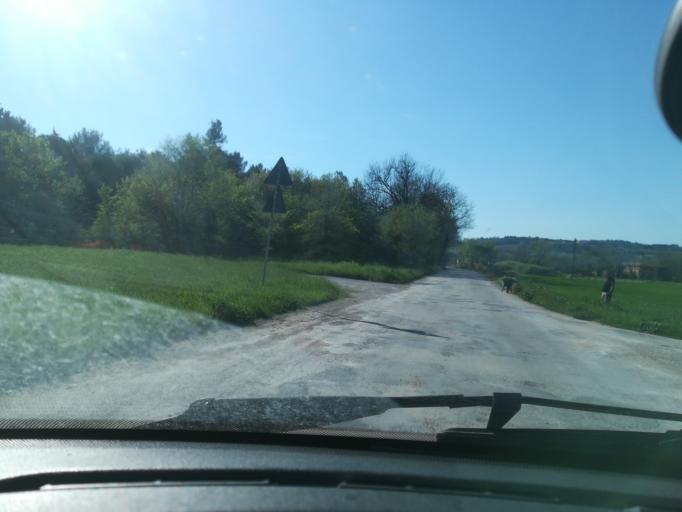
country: IT
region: The Marches
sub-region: Provincia di Macerata
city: Zona Industriale
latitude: 43.2680
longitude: 13.4922
